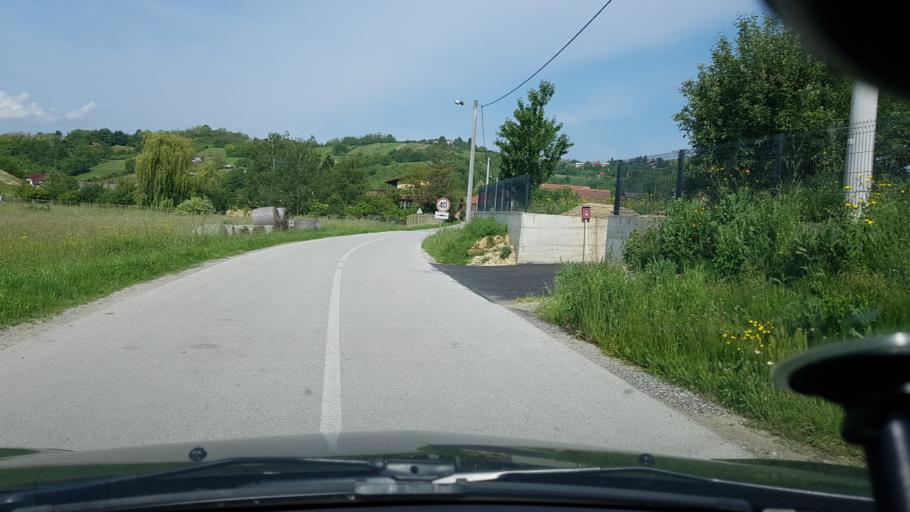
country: HR
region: Krapinsko-Zagorska
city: Marija Bistrica
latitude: 45.9369
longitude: 16.2054
